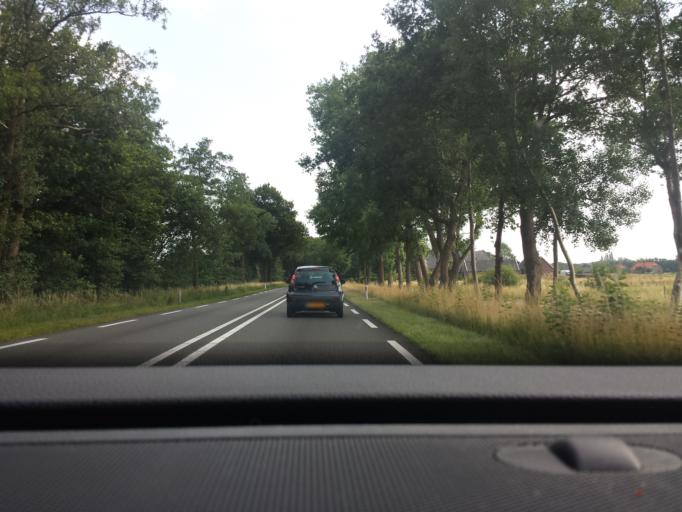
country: NL
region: Gelderland
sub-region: Gemeente Lochem
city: Laren
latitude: 52.1797
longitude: 6.3827
